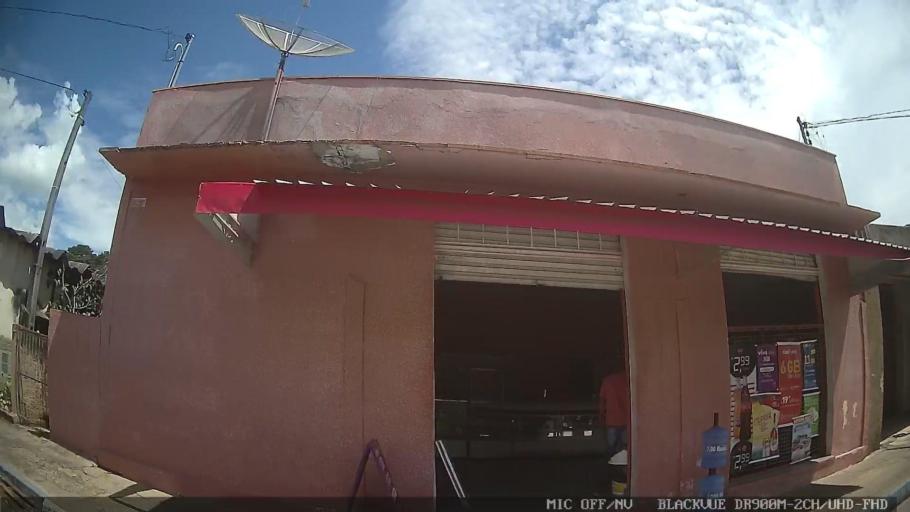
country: BR
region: Sao Paulo
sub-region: Conchas
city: Conchas
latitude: -23.0149
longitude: -48.0129
